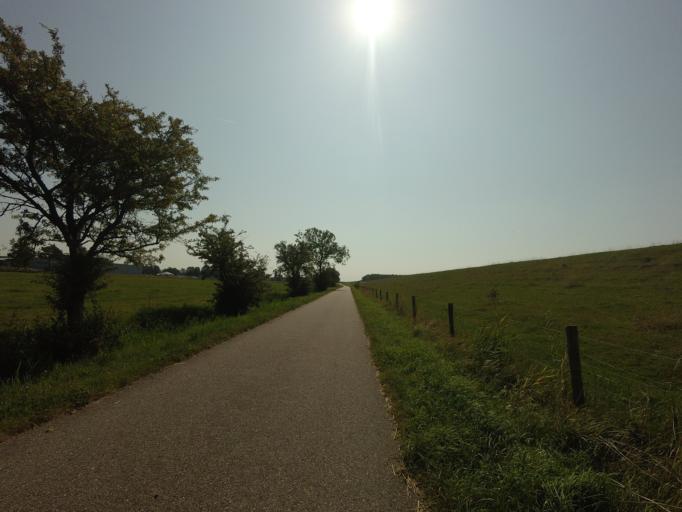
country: NL
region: Groningen
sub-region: Gemeente De Marne
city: Ulrum
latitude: 53.3472
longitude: 6.2972
